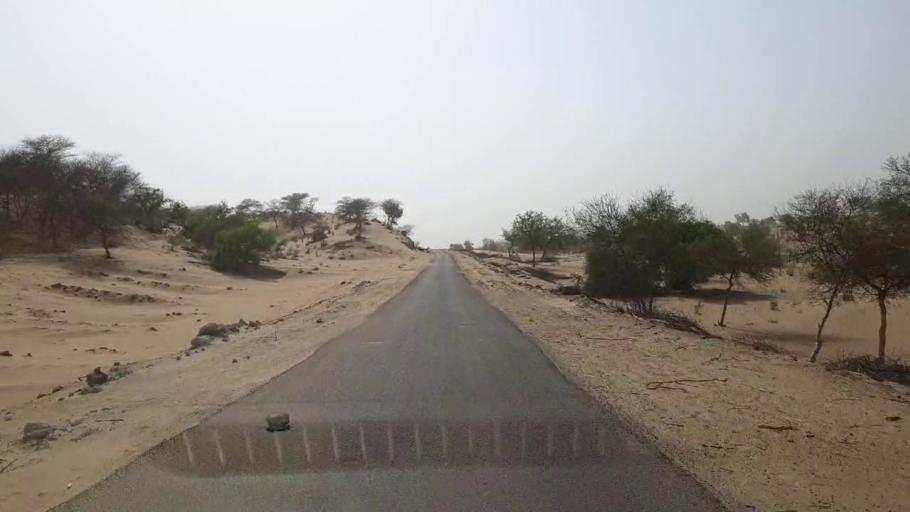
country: PK
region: Sindh
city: Mithi
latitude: 24.6195
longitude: 69.8812
